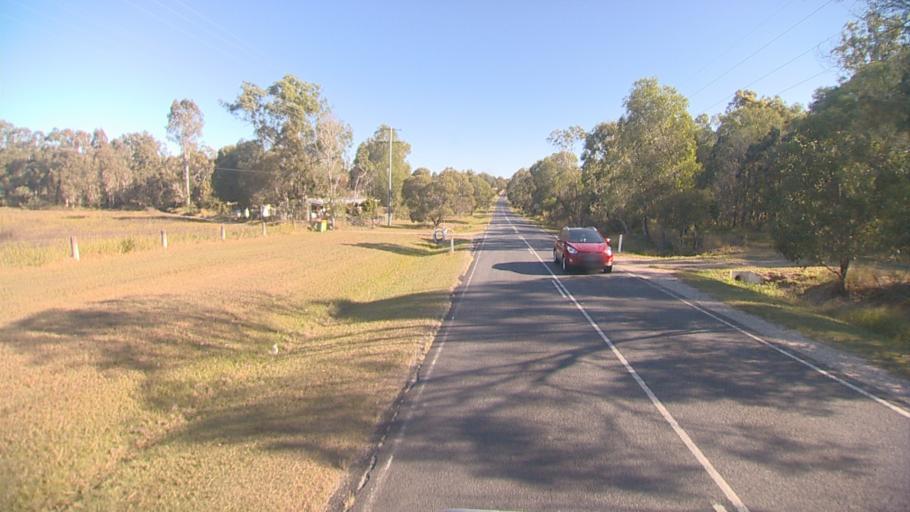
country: AU
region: Queensland
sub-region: Logan
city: North Maclean
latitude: -27.7836
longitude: 153.0523
